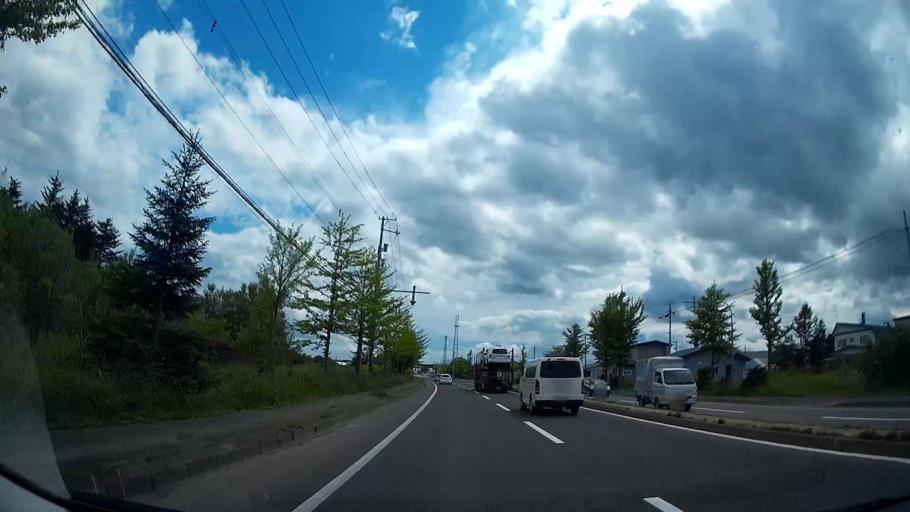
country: JP
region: Hokkaido
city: Kitahiroshima
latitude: 42.8744
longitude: 141.5629
